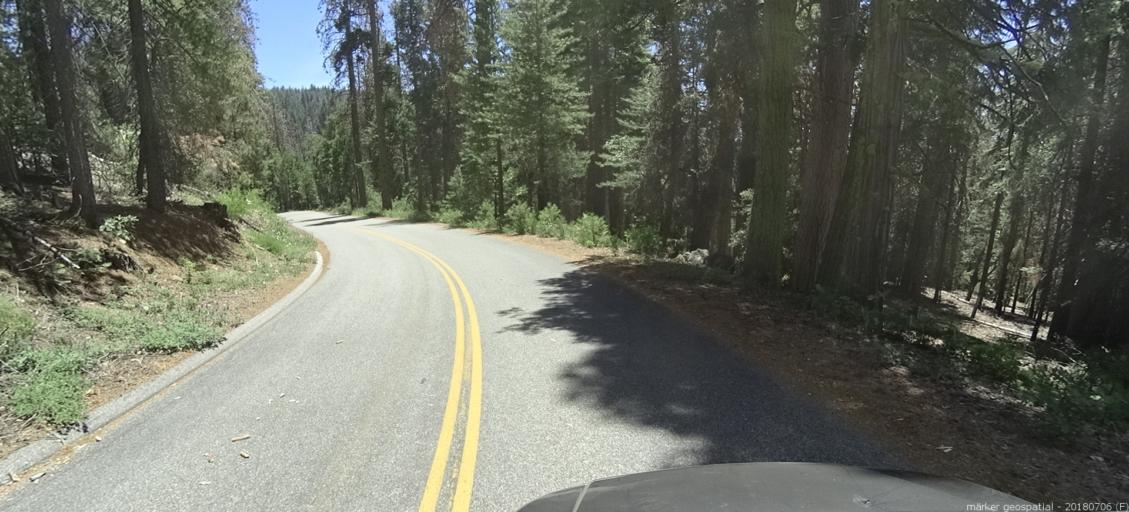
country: US
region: California
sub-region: Madera County
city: Oakhurst
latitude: 37.3783
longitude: -119.5300
